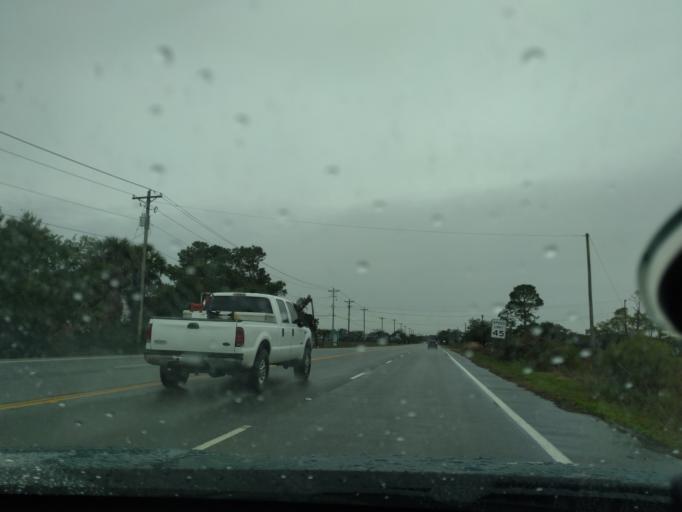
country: US
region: South Carolina
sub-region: Charleston County
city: Folly Beach
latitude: 32.6791
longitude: -79.9544
